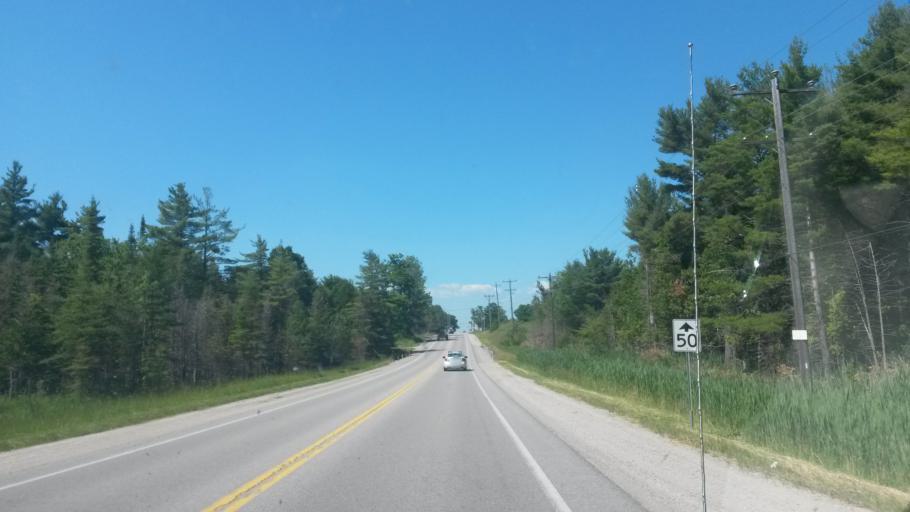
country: CA
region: Ontario
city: Barrie
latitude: 44.5325
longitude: -79.7194
